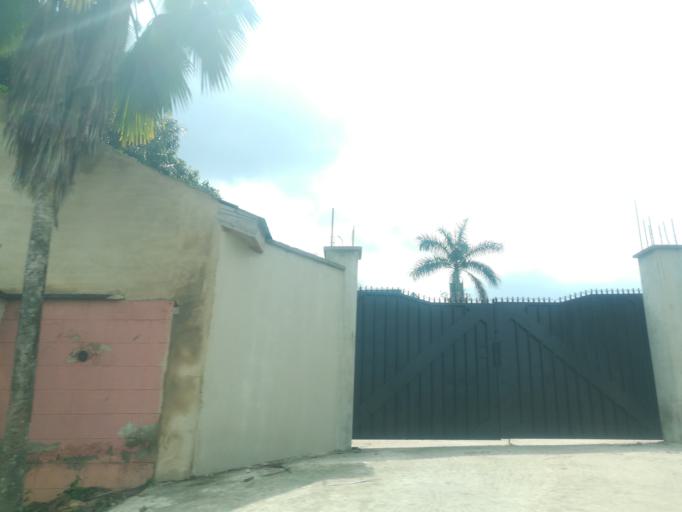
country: NG
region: Oyo
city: Moniya
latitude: 7.4618
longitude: 3.9199
